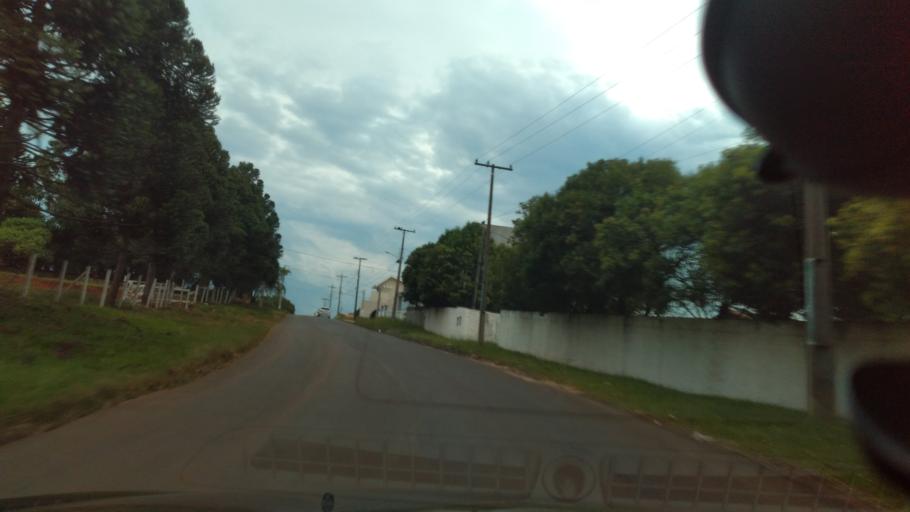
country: BR
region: Parana
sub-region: Guarapuava
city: Guarapuava
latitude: -25.3905
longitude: -51.4854
